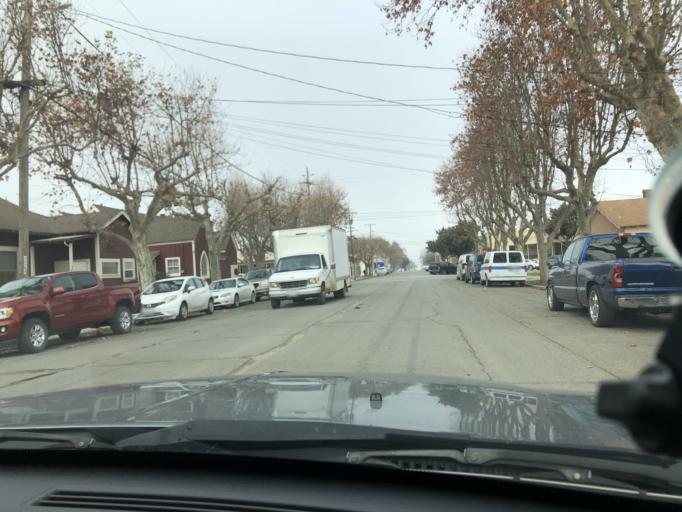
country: US
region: California
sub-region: Monterey County
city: King City
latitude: 36.2116
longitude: -121.1252
